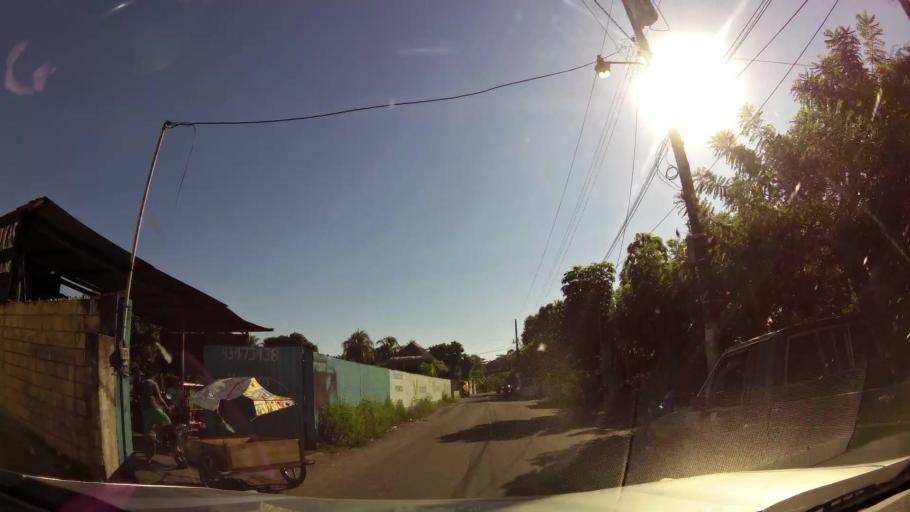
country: GT
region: Santa Rosa
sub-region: Municipio de Taxisco
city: Taxisco
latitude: 13.8925
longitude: -90.4798
